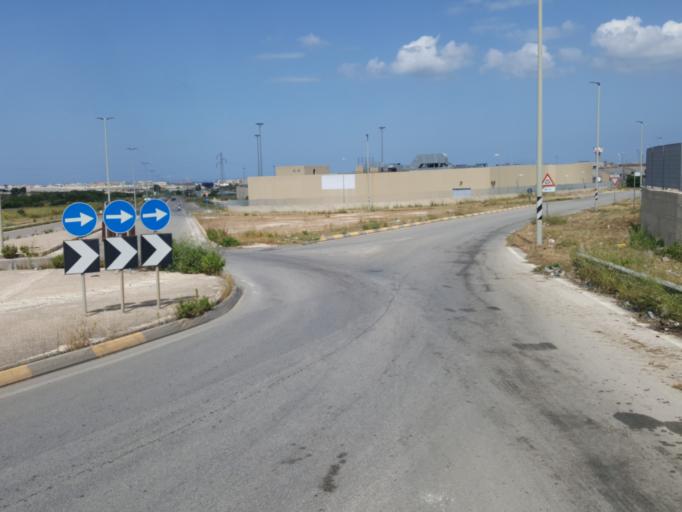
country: IT
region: Apulia
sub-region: Provincia di Bari
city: San Paolo
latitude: 41.1161
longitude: 16.8011
